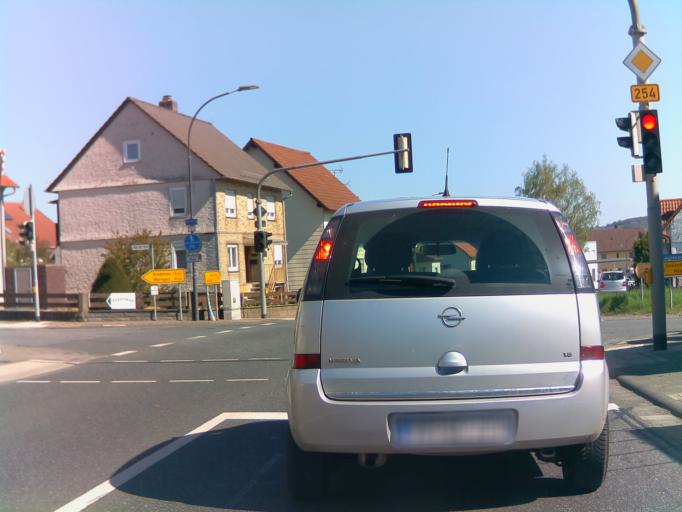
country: DE
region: Hesse
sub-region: Regierungsbezirk Giessen
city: Lauterbach
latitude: 50.6562
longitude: 9.3820
